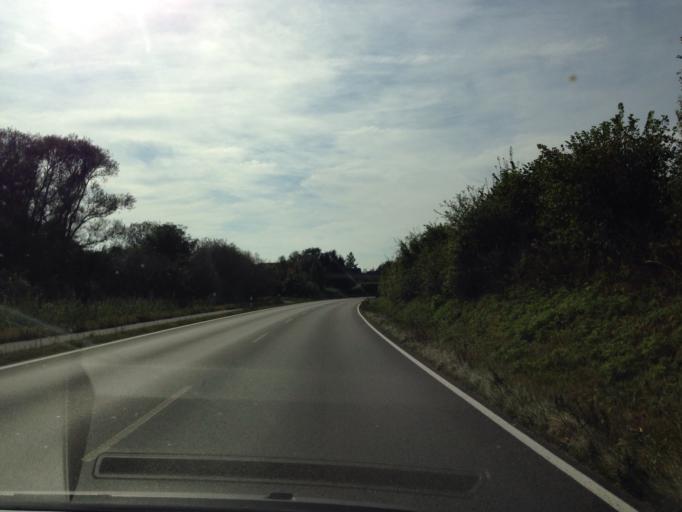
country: DE
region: North Rhine-Westphalia
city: Ludinghausen
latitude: 51.7692
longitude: 7.4672
